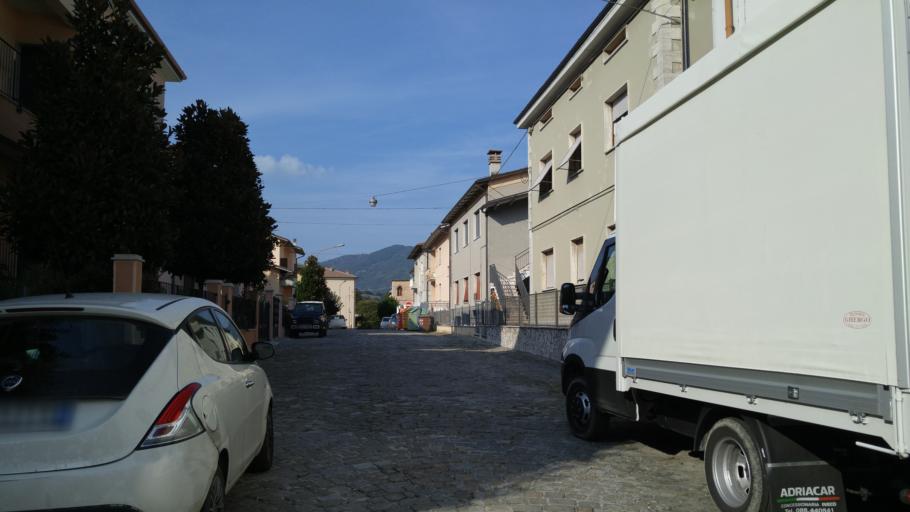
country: IT
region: The Marches
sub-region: Provincia di Pesaro e Urbino
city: Acqualagna
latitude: 43.6186
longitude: 12.6726
